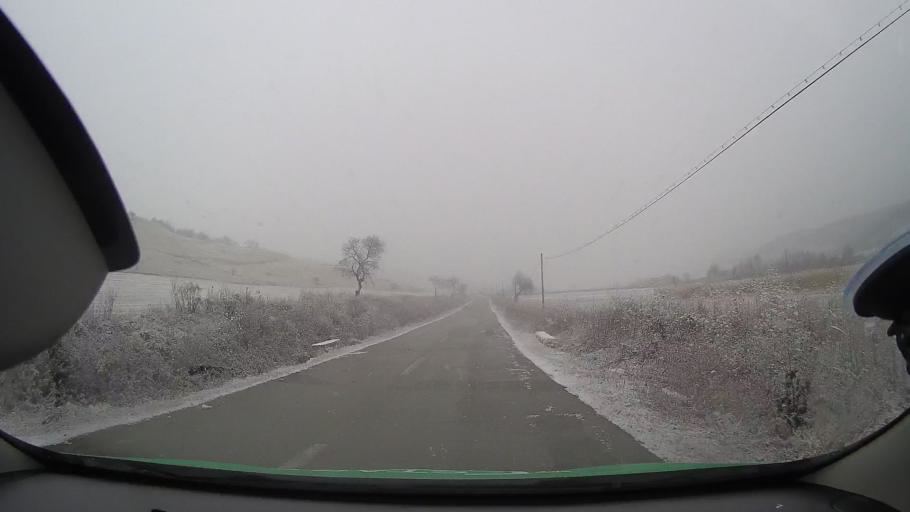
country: RO
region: Alba
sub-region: Comuna Lopadea Noua
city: Lopadea Noua
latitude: 46.2991
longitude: 23.8437
